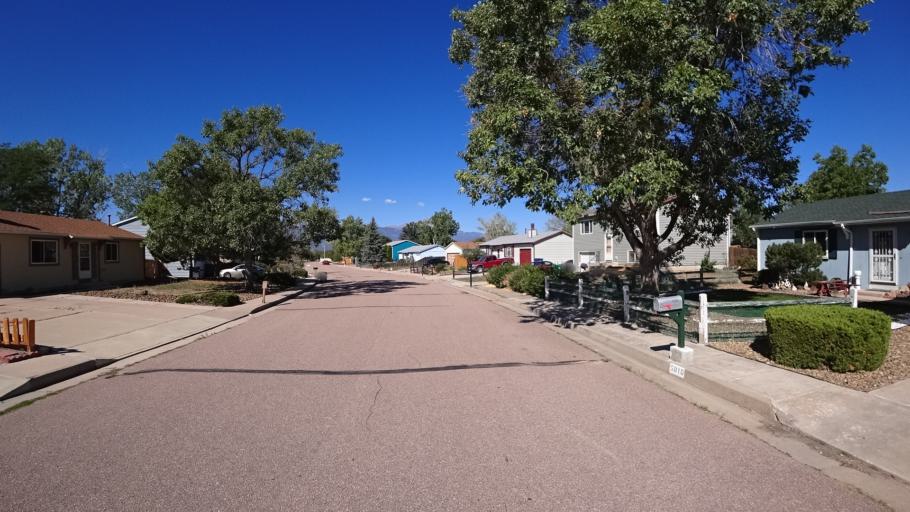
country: US
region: Colorado
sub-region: El Paso County
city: Cimarron Hills
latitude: 38.8189
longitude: -104.7344
